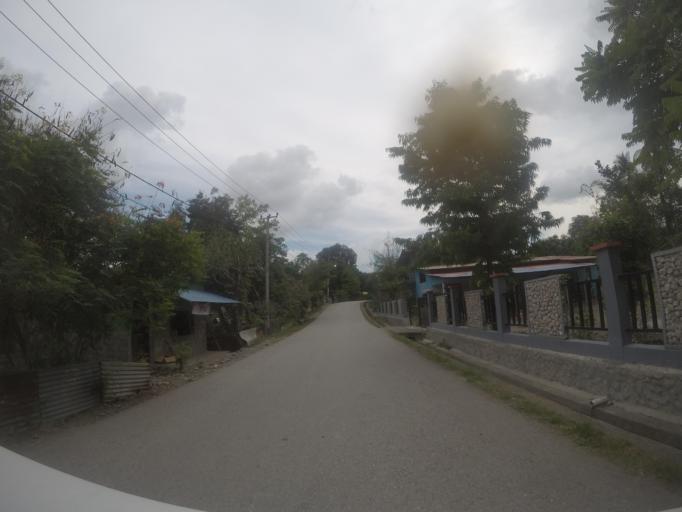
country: TL
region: Viqueque
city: Viqueque
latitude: -8.8687
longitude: 126.3674
